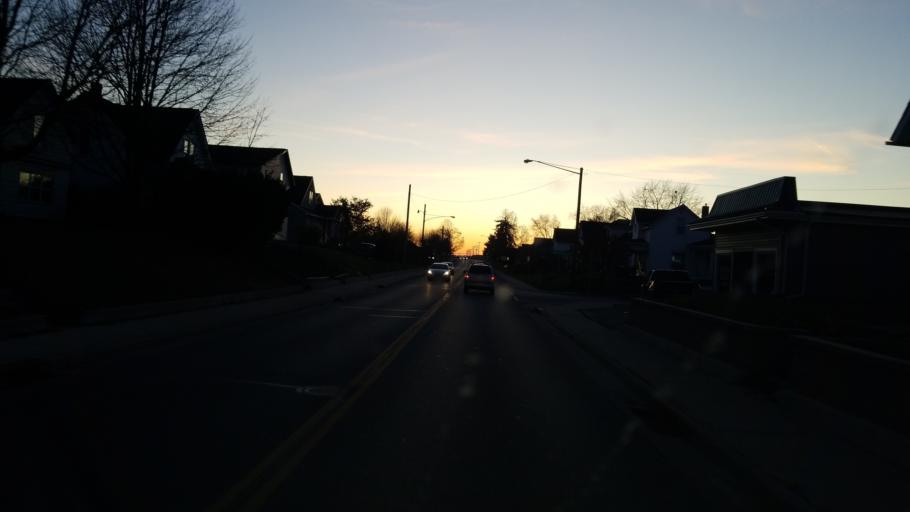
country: US
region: Ohio
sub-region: Fayette County
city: Washington Court House
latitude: 39.5305
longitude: -83.4481
